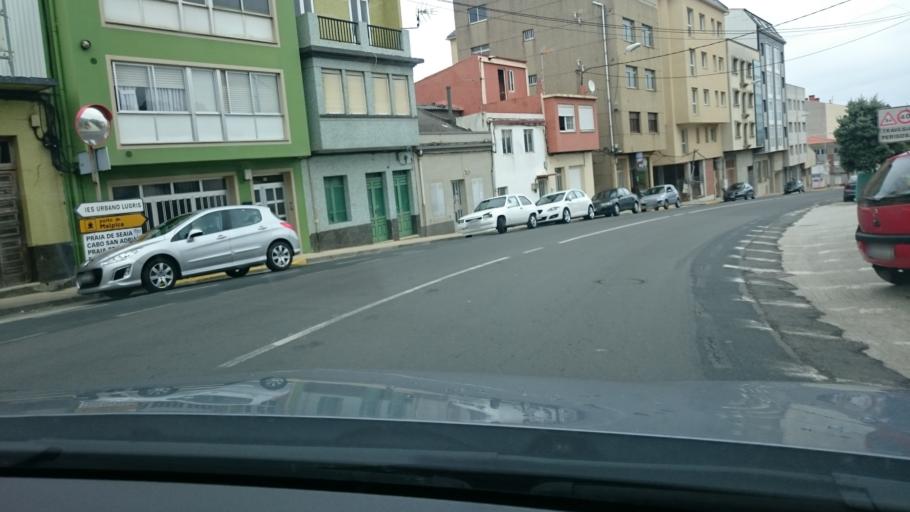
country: ES
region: Galicia
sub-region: Provincia da Coruna
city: Malpica
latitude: 43.3200
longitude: -8.8196
